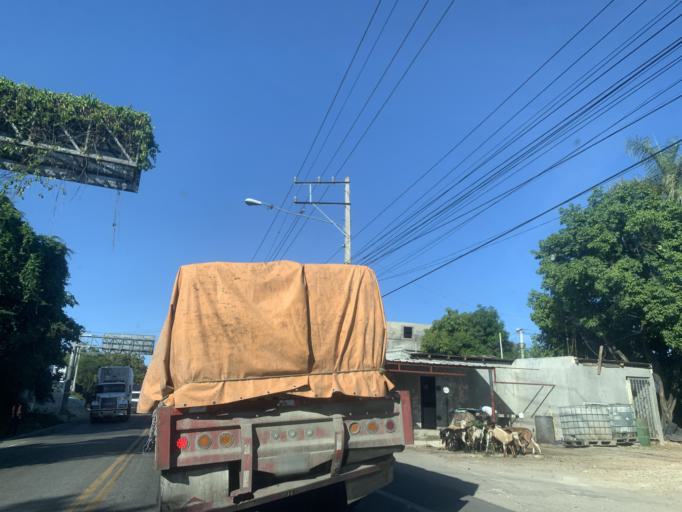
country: DO
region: San Cristobal
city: Bajos de Haina
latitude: 18.4261
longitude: -70.0368
